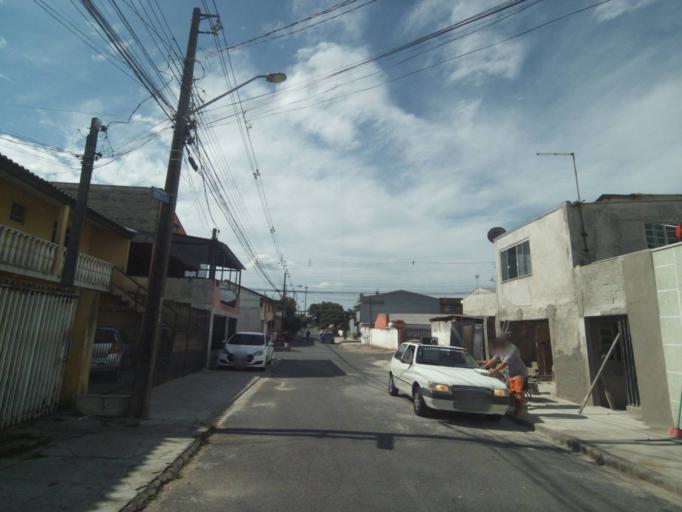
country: BR
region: Parana
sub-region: Curitiba
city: Curitiba
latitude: -25.5157
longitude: -49.3318
